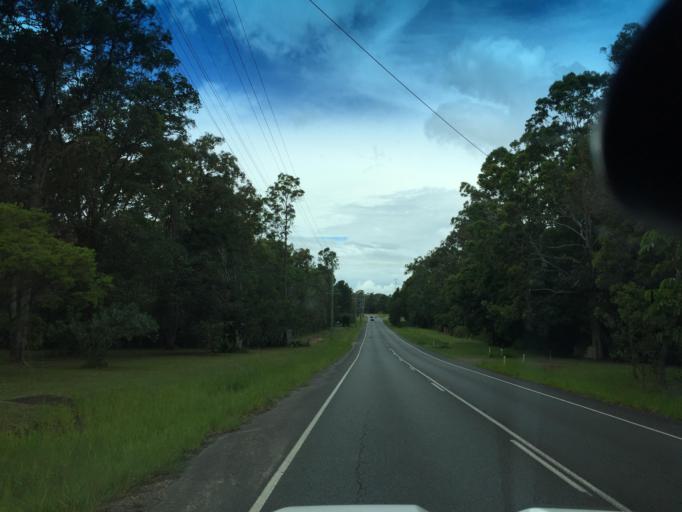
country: AU
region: Queensland
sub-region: Moreton Bay
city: Caboolture
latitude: -27.0648
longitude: 152.9120
